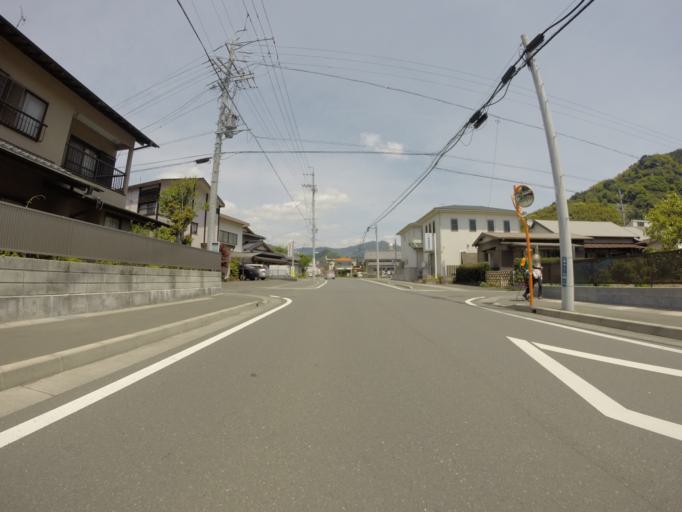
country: JP
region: Shizuoka
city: Shizuoka-shi
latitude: 35.0201
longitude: 138.4229
